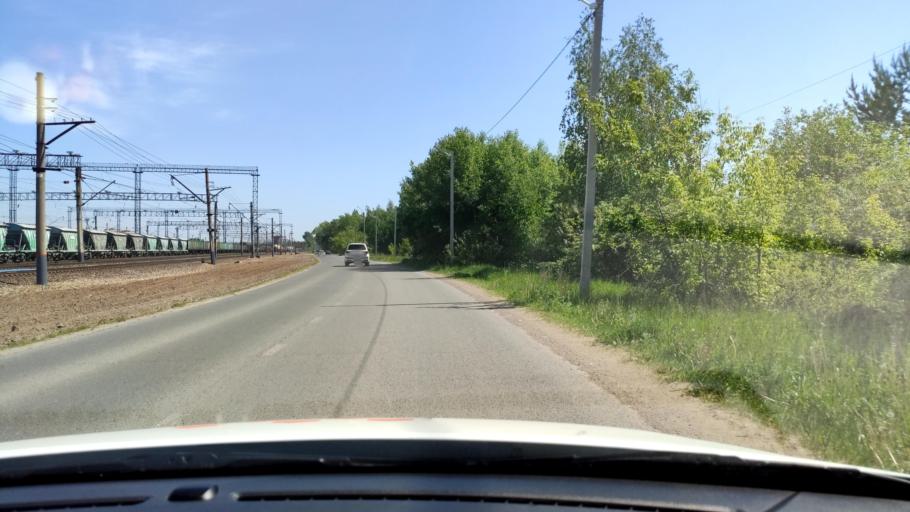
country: RU
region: Tatarstan
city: Osinovo
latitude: 55.8226
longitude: 48.8507
